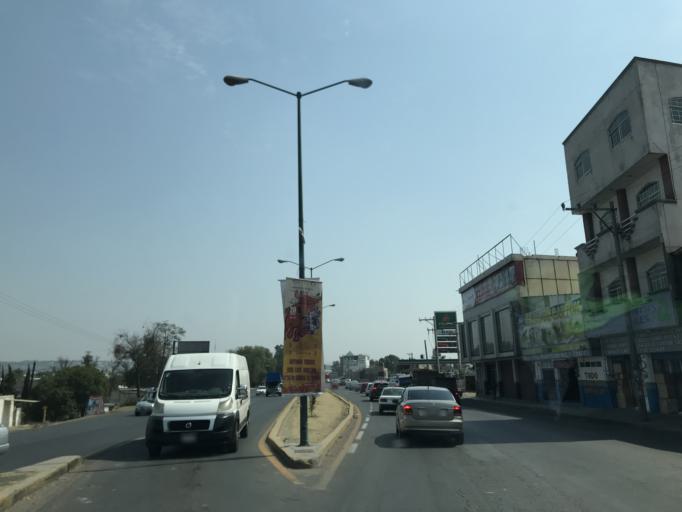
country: MX
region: Tlaxcala
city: Tlaxcala de Xicohtencatl
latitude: 19.3191
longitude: -98.2024
